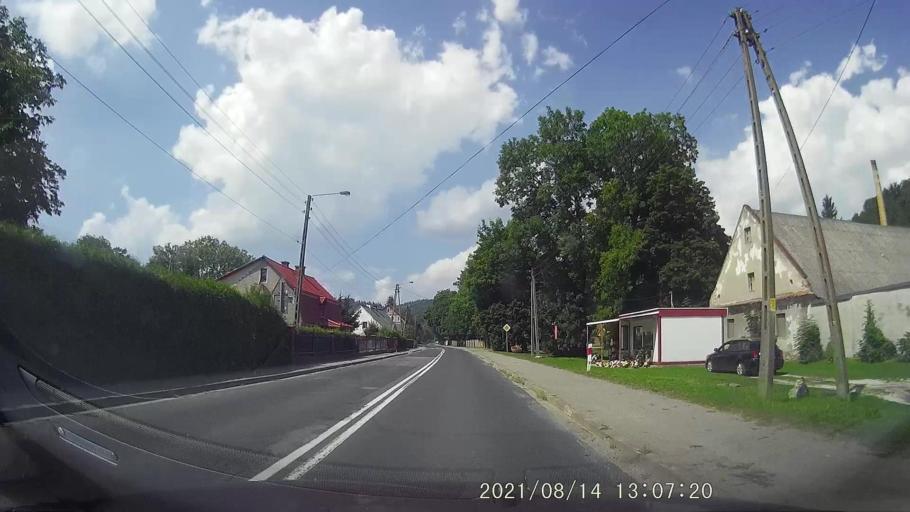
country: PL
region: Lower Silesian Voivodeship
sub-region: Powiat klodzki
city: Klodzko
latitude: 50.3667
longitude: 16.7089
